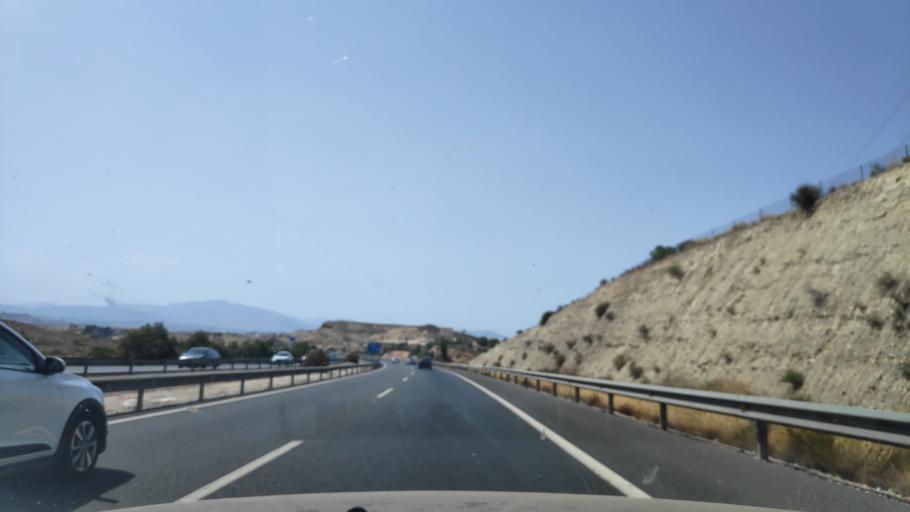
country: ES
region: Murcia
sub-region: Murcia
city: Molina de Segura
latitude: 38.0524
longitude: -1.1770
